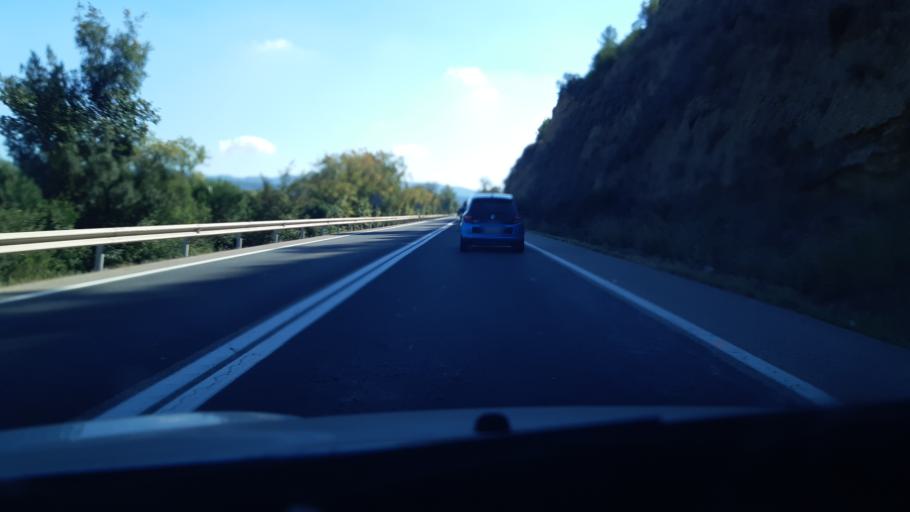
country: ES
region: Catalonia
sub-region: Provincia de Tarragona
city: Tivenys
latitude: 40.8612
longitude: 0.5088
